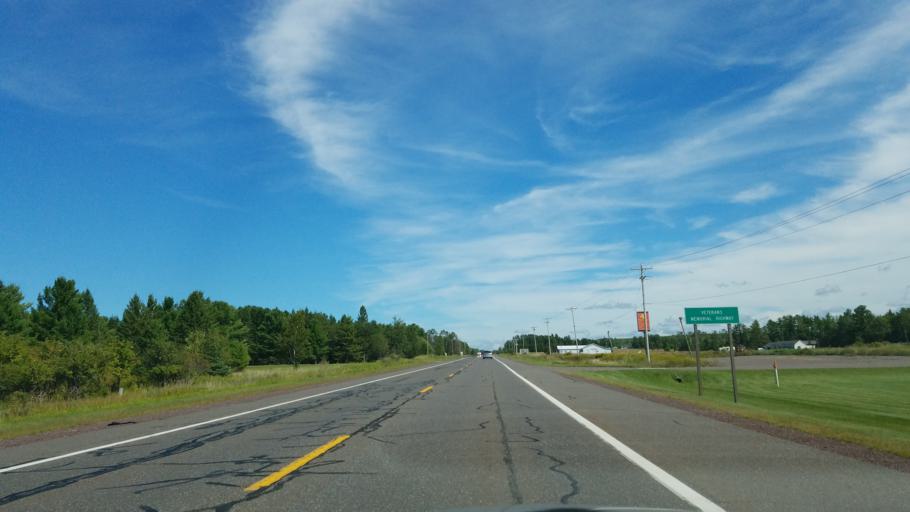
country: US
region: Michigan
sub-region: Ontonagon County
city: Ontonagon
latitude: 46.5348
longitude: -89.1691
